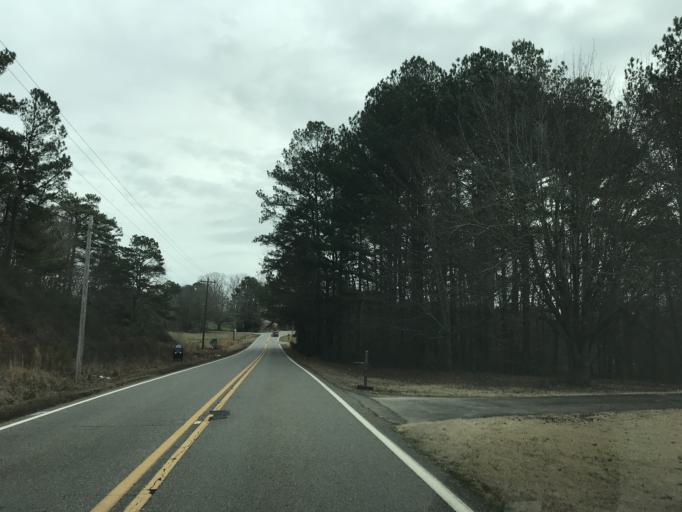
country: US
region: Georgia
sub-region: Fulton County
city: Milton
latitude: 34.1957
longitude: -84.3453
